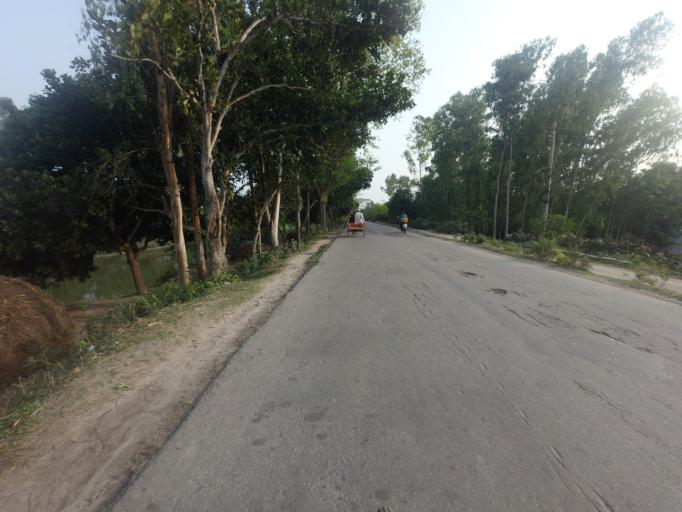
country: BD
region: Rajshahi
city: Sirajganj
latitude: 24.3204
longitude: 89.6977
